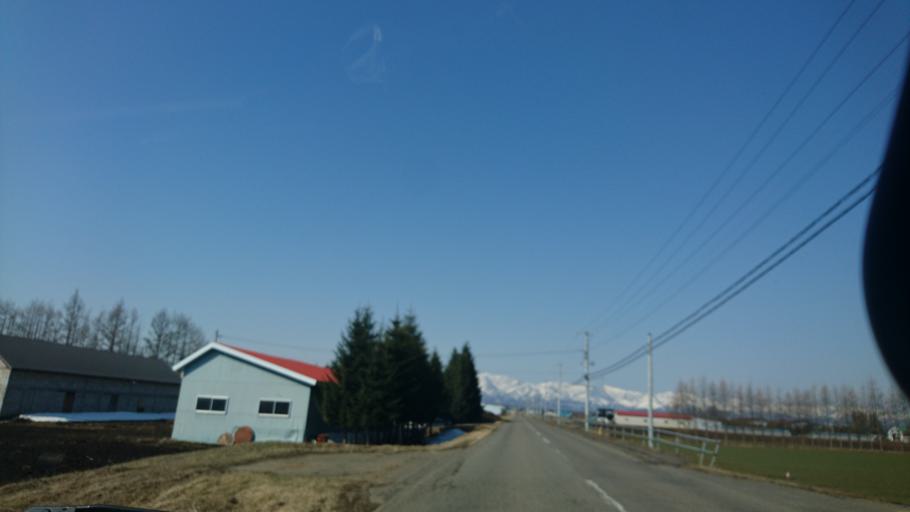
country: JP
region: Hokkaido
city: Obihiro
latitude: 42.9038
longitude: 143.0907
